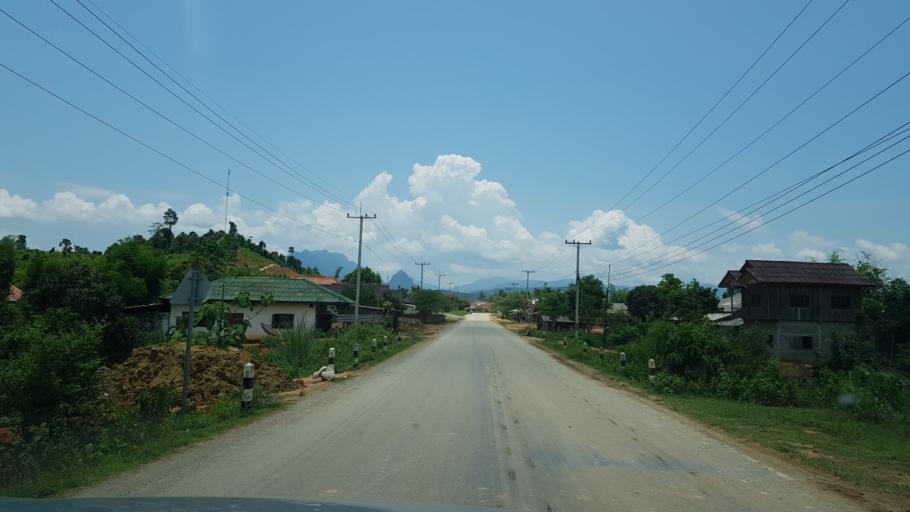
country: LA
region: Vientiane
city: Muang Kasi
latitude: 19.2700
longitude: 102.2274
